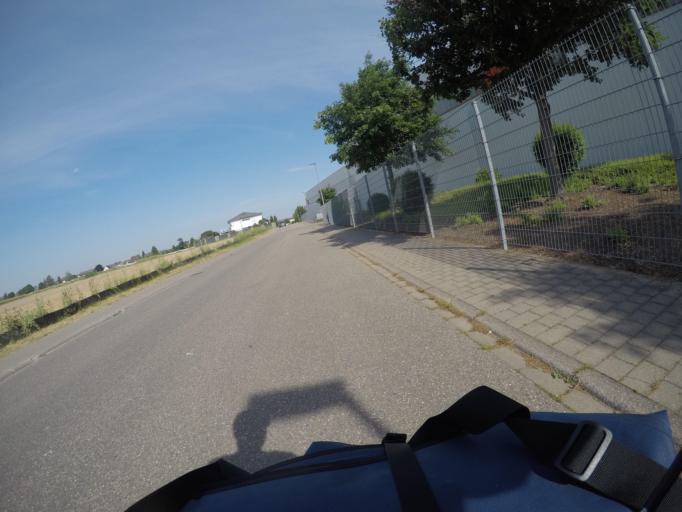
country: DE
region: Baden-Wuerttemberg
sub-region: Karlsruhe Region
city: Bietigheim
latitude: 48.9069
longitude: 8.2603
